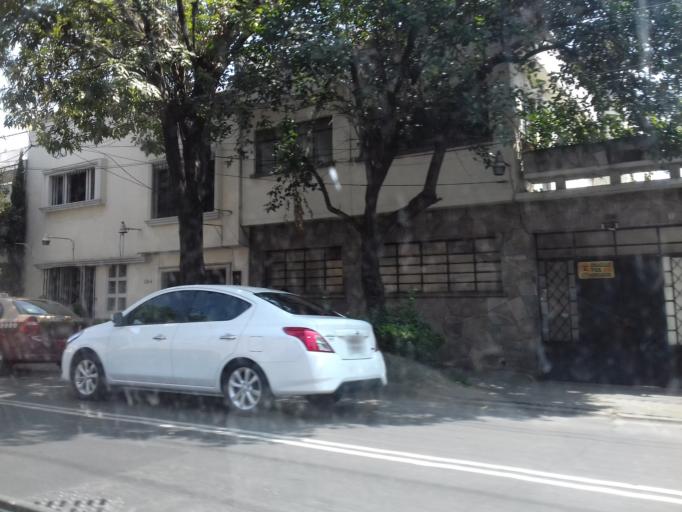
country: MX
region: Mexico City
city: Colonia del Valle
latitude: 19.3764
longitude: -99.1666
